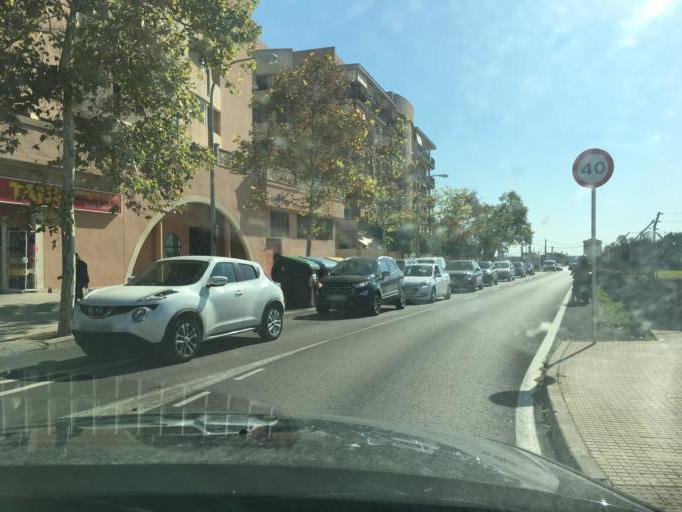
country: ES
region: Balearic Islands
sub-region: Illes Balears
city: Palma
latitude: 39.5822
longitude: 2.6829
